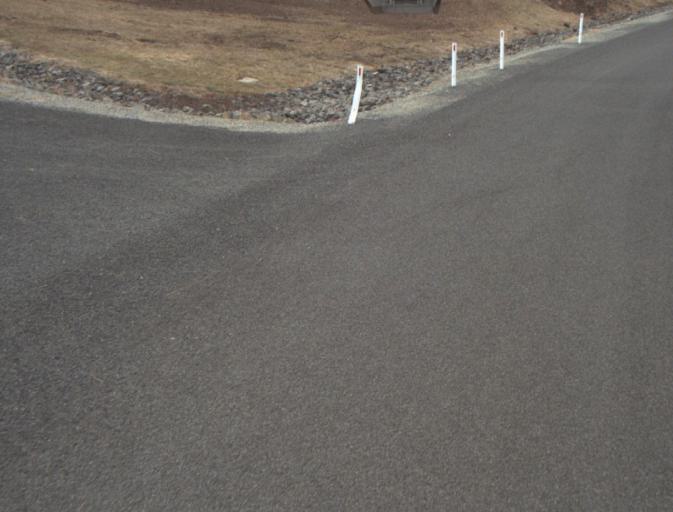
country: AU
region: Tasmania
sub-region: Launceston
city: Mayfield
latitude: -41.3019
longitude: 147.0420
